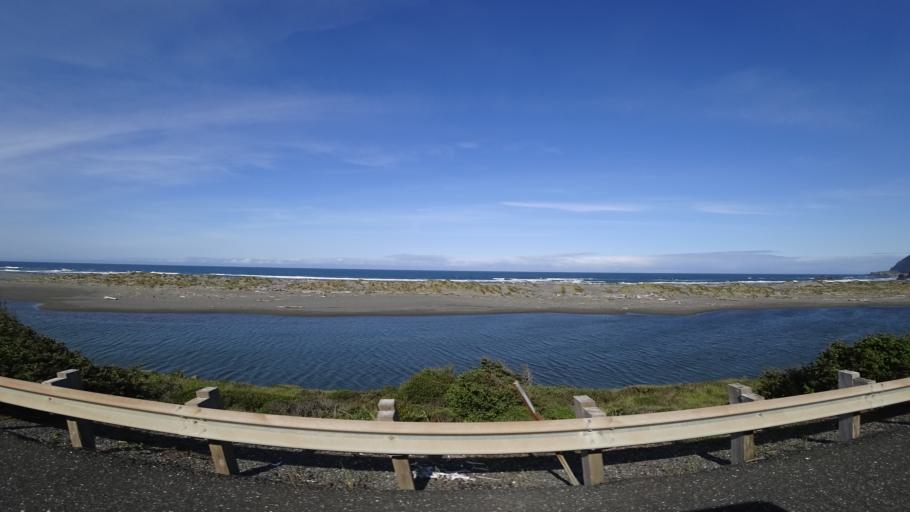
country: US
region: Oregon
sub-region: Curry County
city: Gold Beach
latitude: 42.2858
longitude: -124.4049
